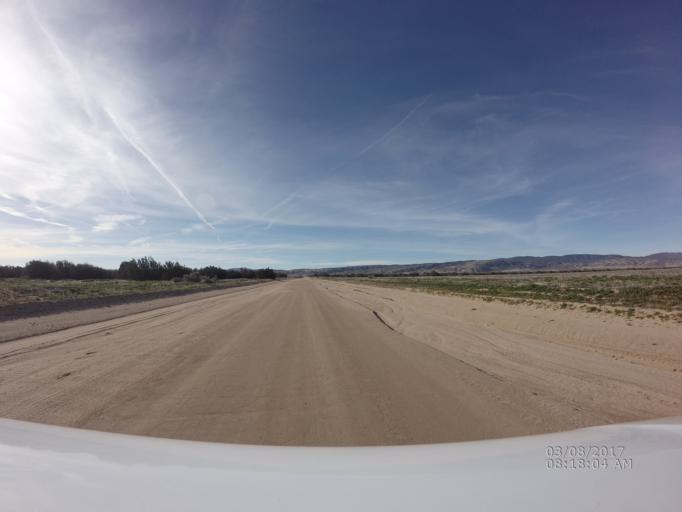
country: US
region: California
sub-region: Los Angeles County
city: Green Valley
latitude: 34.7703
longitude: -118.4489
